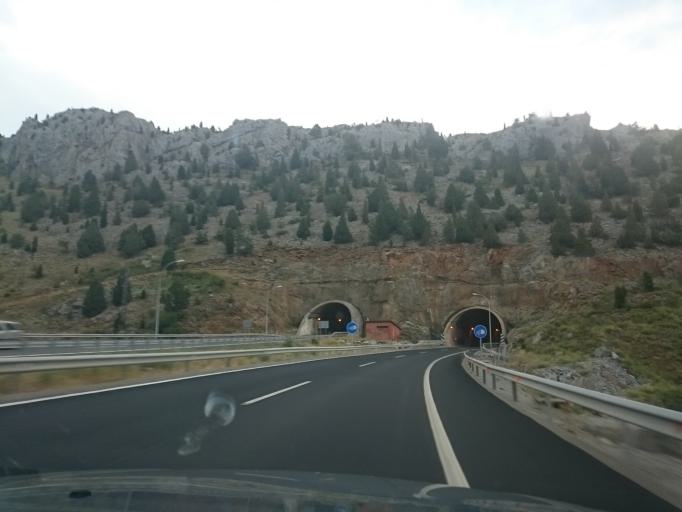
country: ES
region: Castille and Leon
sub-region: Provincia de Leon
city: Sena de Luna
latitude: 42.8841
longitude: -5.8920
